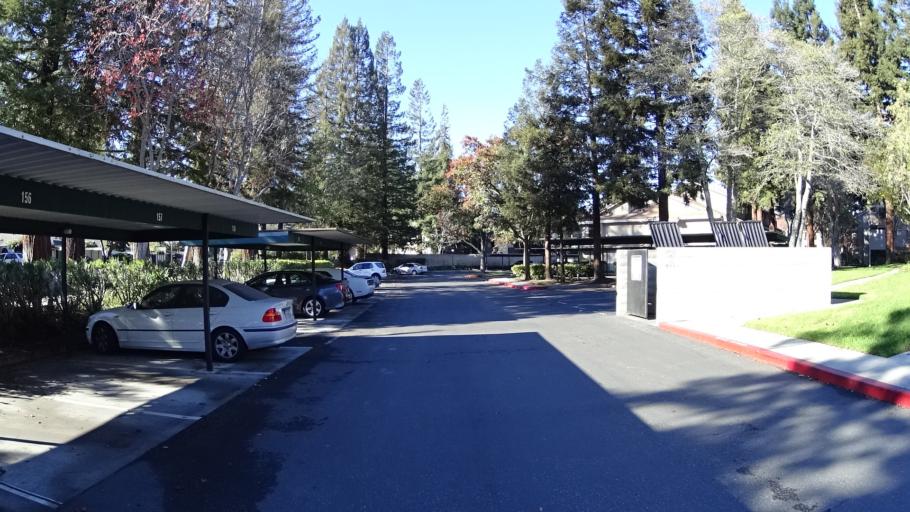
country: US
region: California
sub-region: Santa Clara County
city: Sunnyvale
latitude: 37.3696
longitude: -122.0046
